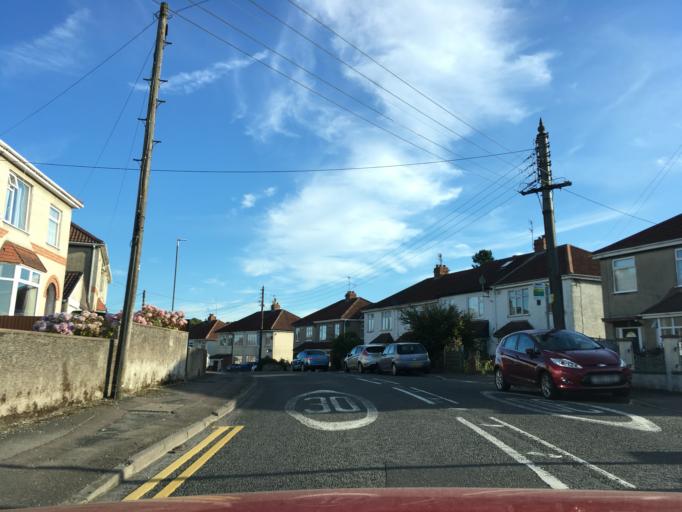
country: GB
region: England
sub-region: South Gloucestershire
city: Mangotsfield
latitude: 51.4775
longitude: -2.4959
